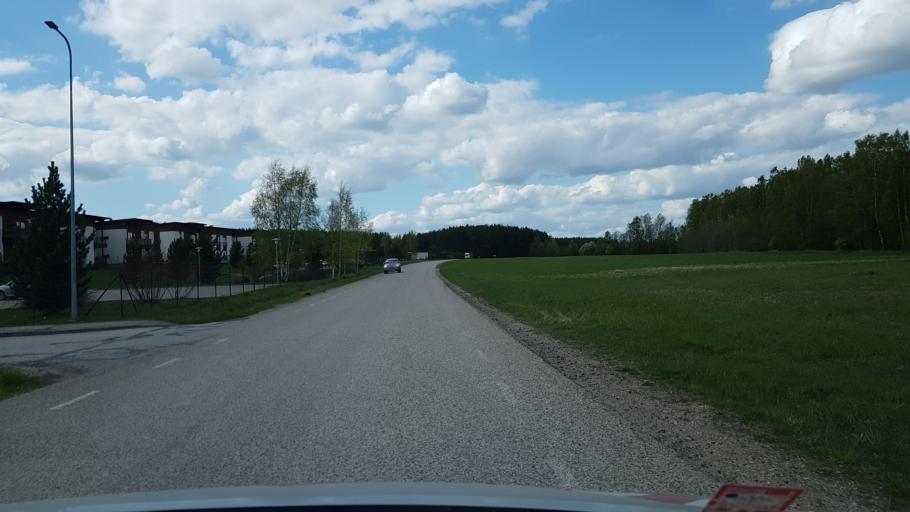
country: EE
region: Tartu
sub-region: Tartu linn
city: Tartu
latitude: 58.3540
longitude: 26.8017
